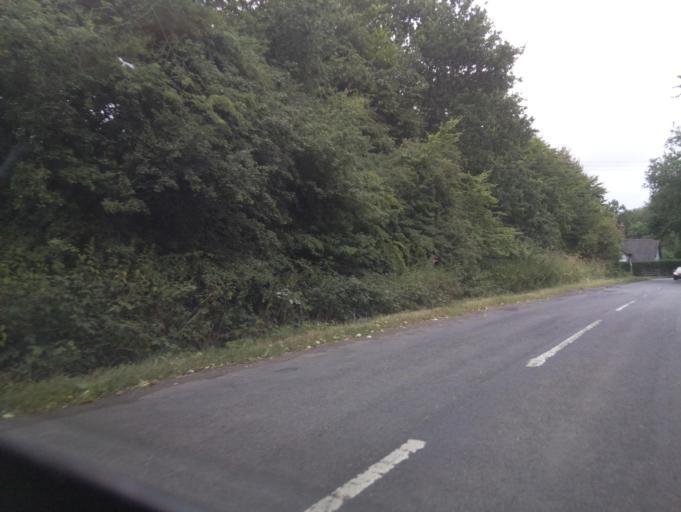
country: GB
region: England
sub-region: Derbyshire
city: Swadlincote
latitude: 52.7921
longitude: -1.5362
